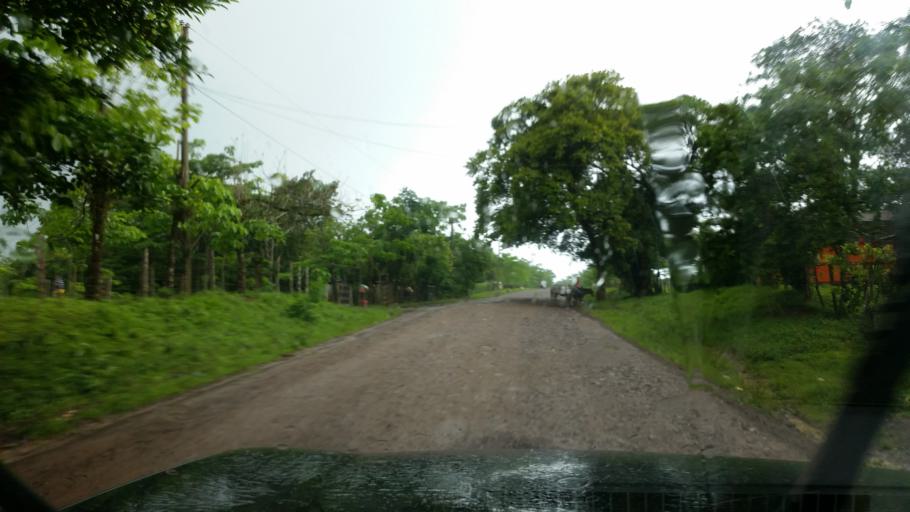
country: NI
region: Atlantico Norte (RAAN)
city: Siuna
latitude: 13.4002
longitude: -84.8541
